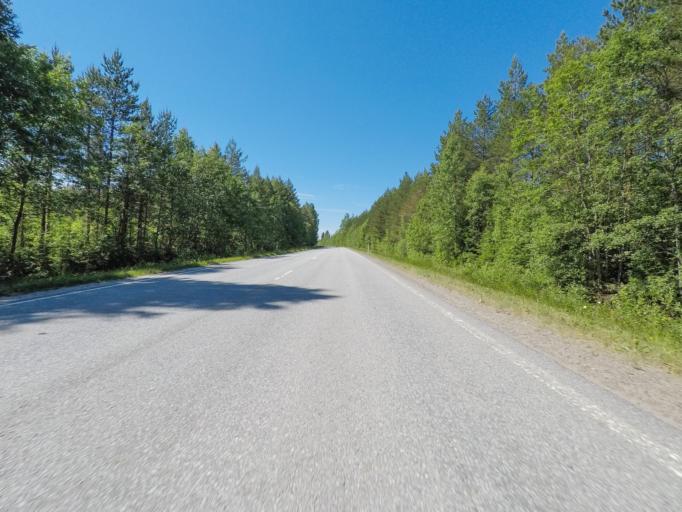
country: FI
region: Southern Savonia
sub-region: Savonlinna
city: Rantasalmi
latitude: 62.0008
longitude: 28.4478
